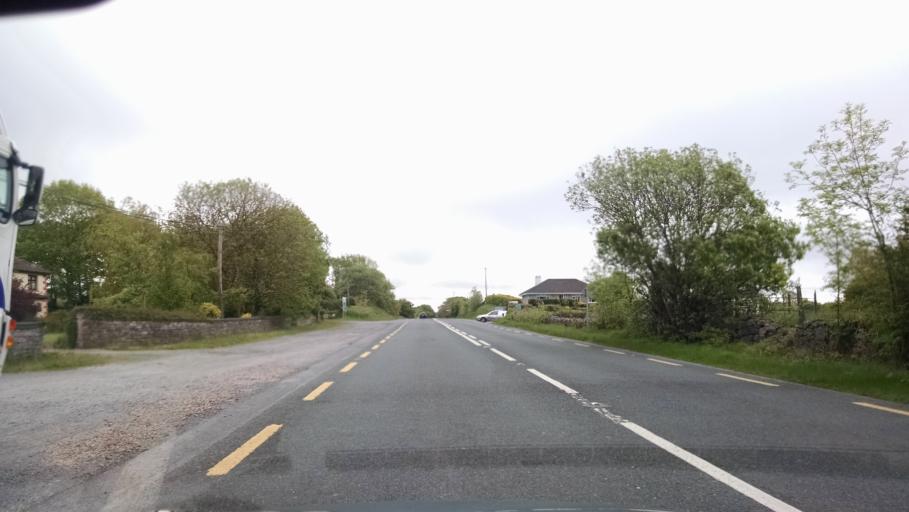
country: IE
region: Connaught
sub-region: County Galway
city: Claregalway
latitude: 53.4175
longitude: -9.0278
